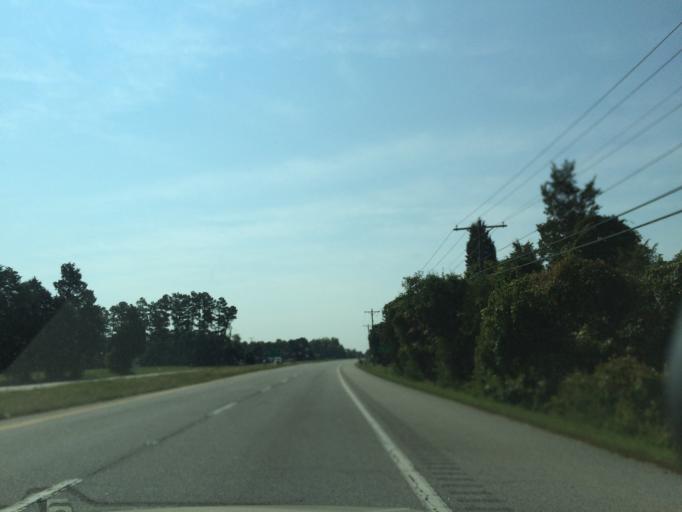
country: US
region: Maryland
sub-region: Charles County
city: La Plata
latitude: 38.4129
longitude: -76.9562
